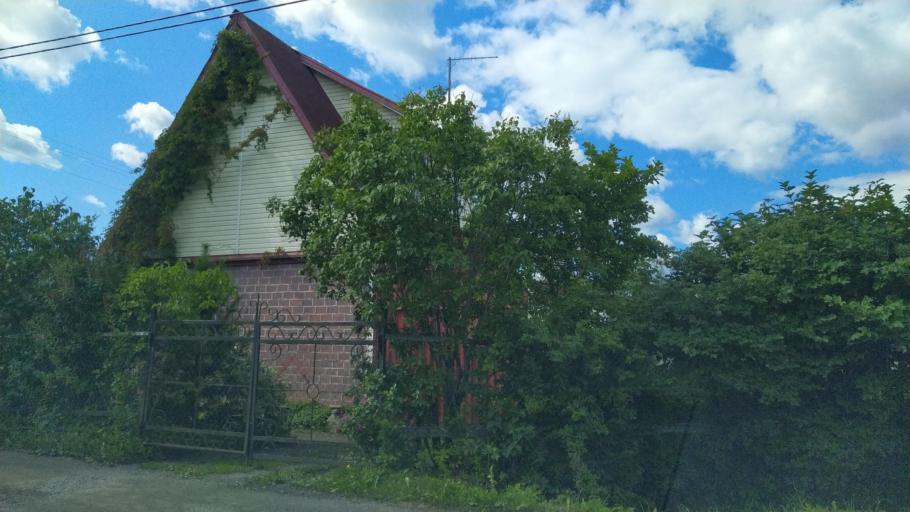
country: RU
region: Leningrad
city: Priozersk
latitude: 61.0037
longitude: 30.1743
